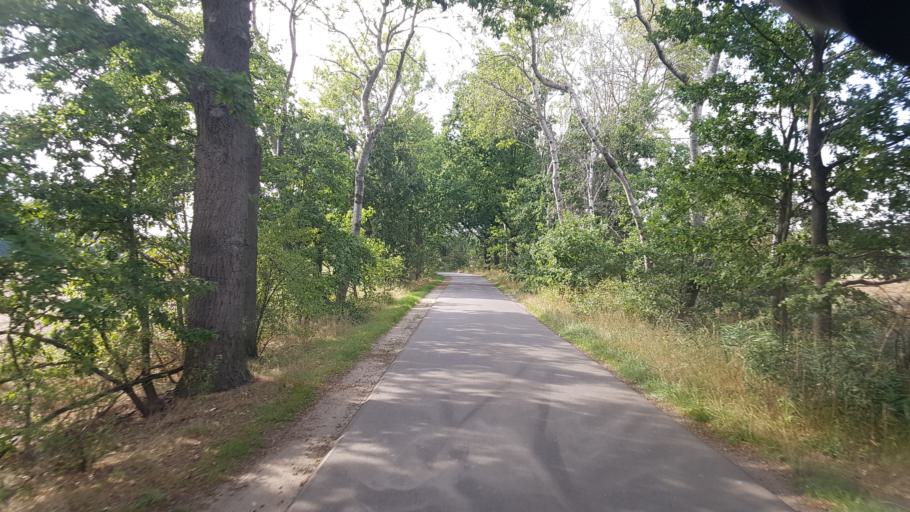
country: DE
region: Brandenburg
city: Plessa
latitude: 51.4391
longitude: 13.6138
